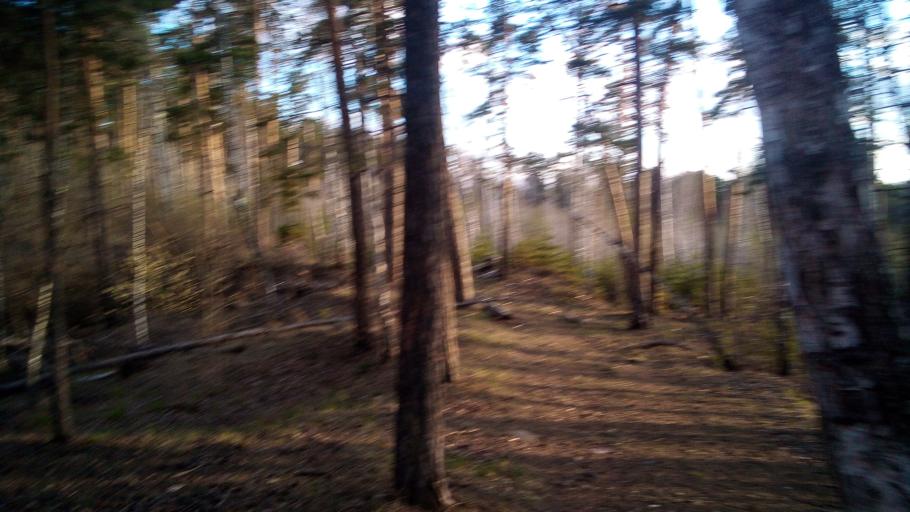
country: RU
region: Chelyabinsk
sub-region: Gorod Chelyabinsk
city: Chelyabinsk
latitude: 55.1626
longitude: 61.3229
